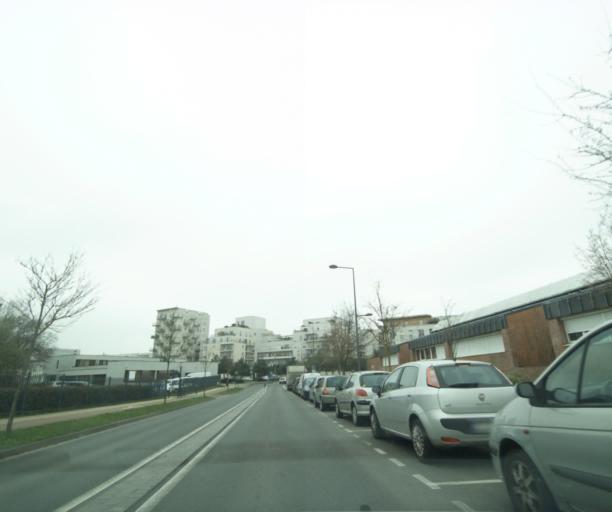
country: FR
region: Ile-de-France
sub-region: Departement du Val-d'Oise
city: Courdimanche
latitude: 49.0477
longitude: 2.0165
